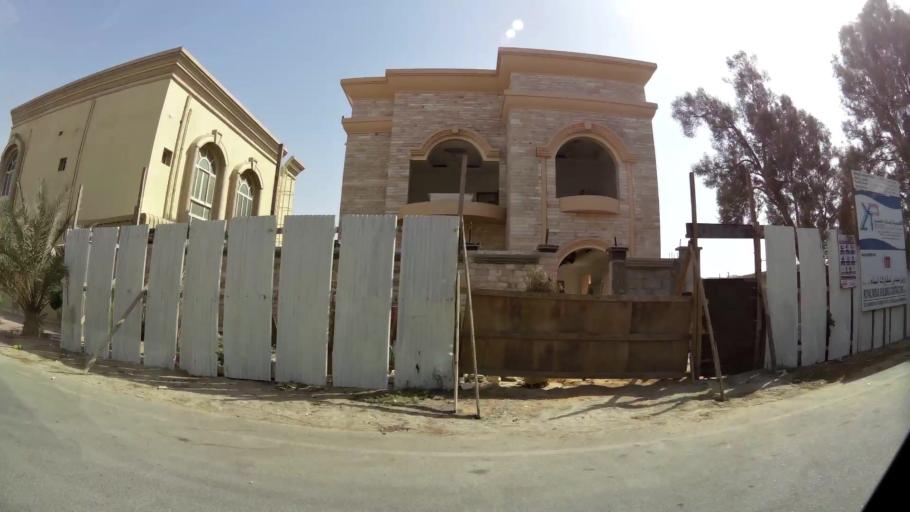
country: AE
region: Dubai
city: Dubai
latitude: 25.1634
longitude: 55.2511
